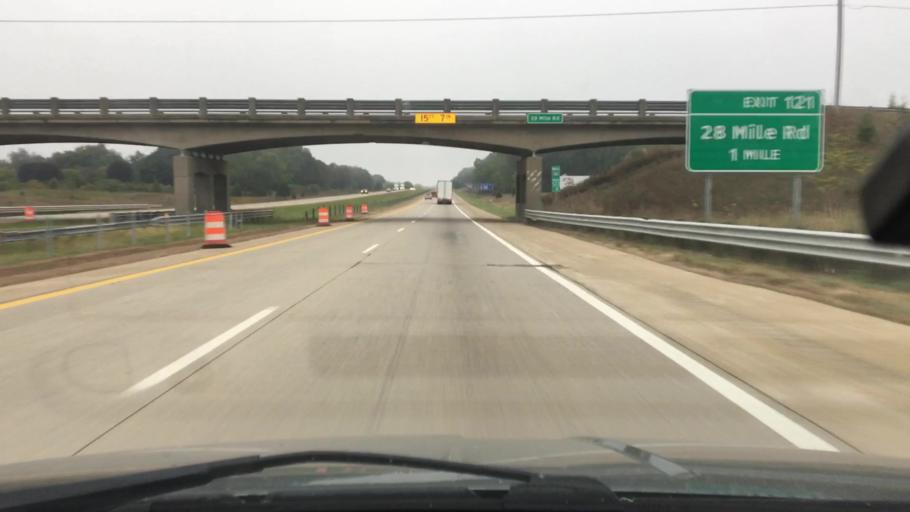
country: US
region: Michigan
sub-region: Calhoun County
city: Albion
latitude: 42.2647
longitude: -84.7362
